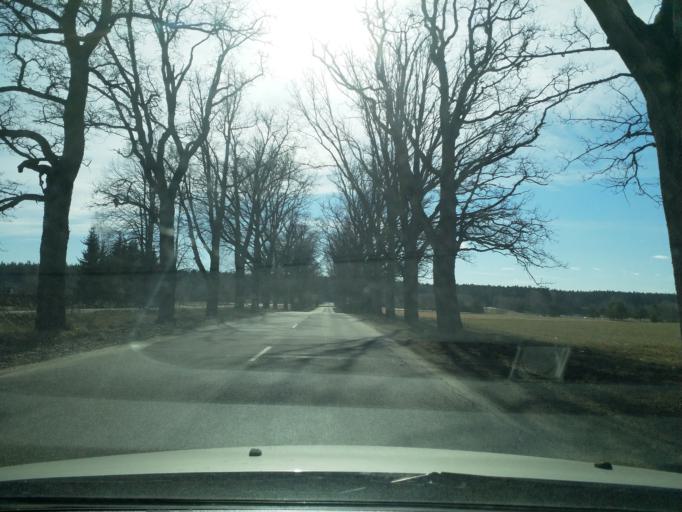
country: LV
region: Valmieras Rajons
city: Valmiera
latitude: 57.5153
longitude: 25.4213
